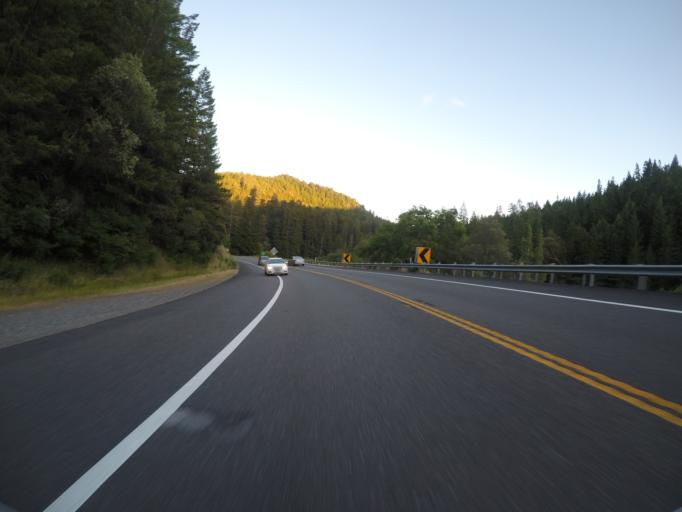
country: US
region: California
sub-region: Humboldt County
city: Redway
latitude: 39.9009
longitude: -123.7546
